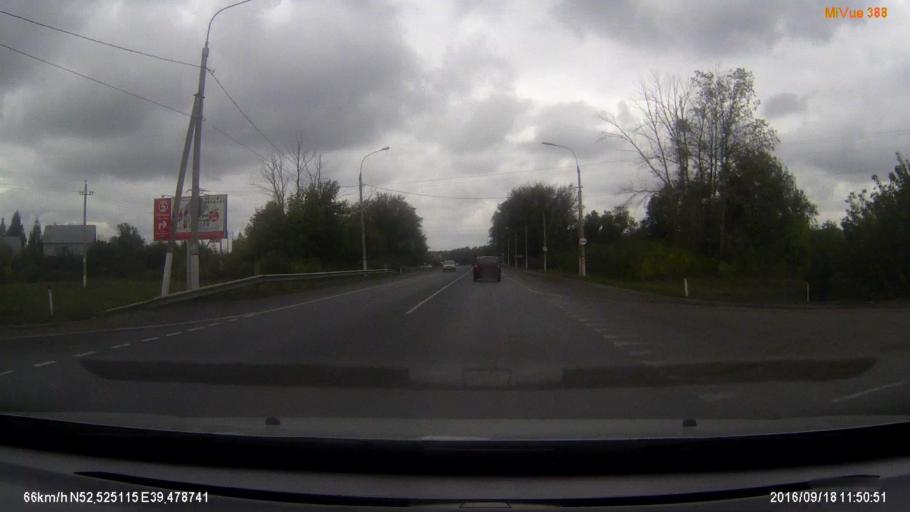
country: RU
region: Lipetsk
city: Syrskoye
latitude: 52.5254
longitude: 39.4791
